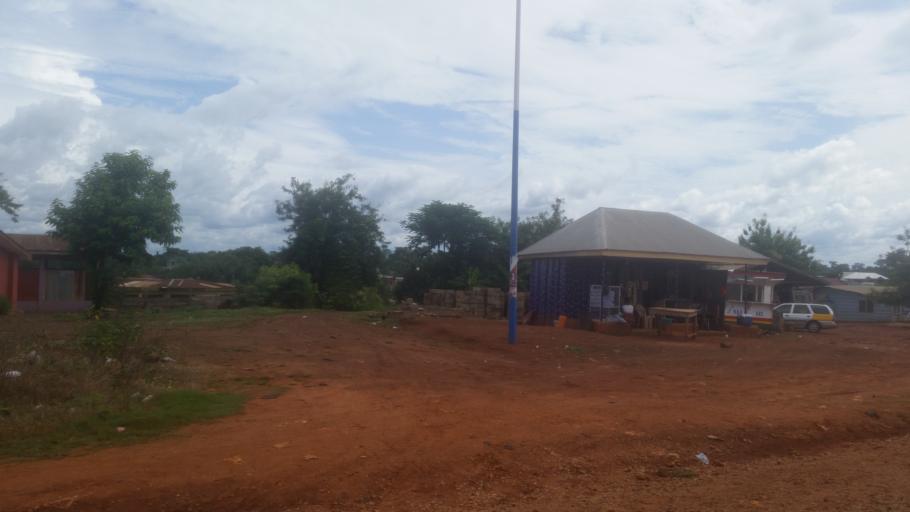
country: GH
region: Western
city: Bibiani
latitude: 6.8066
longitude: -2.5240
